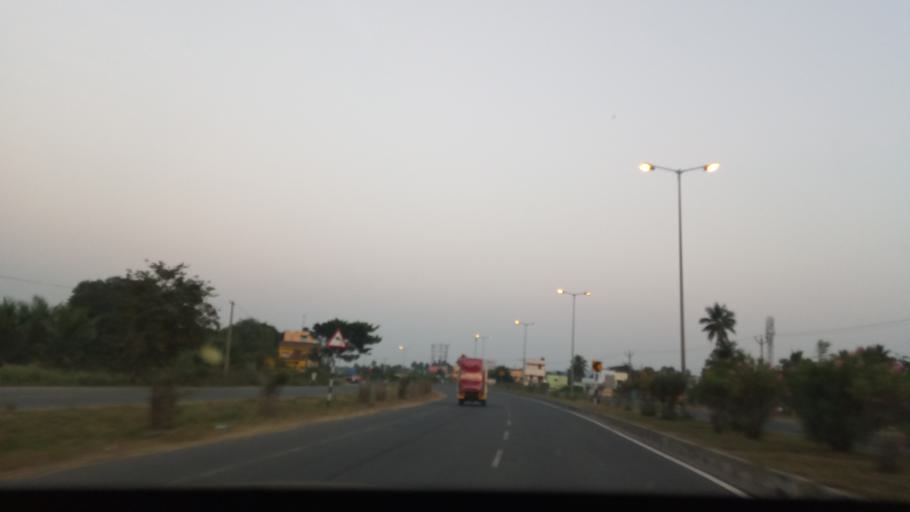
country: IN
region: Tamil Nadu
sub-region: Salem
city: Belur
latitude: 11.6519
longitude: 78.3490
